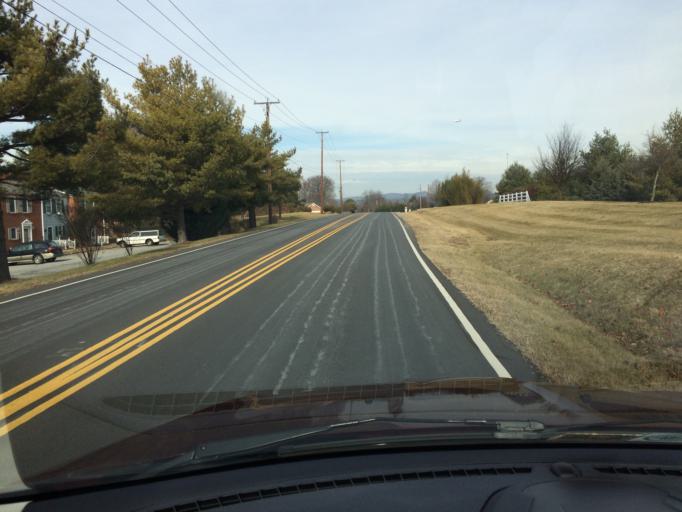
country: US
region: Virginia
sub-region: Roanoke County
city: Hollins
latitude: 37.3358
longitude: -79.9411
